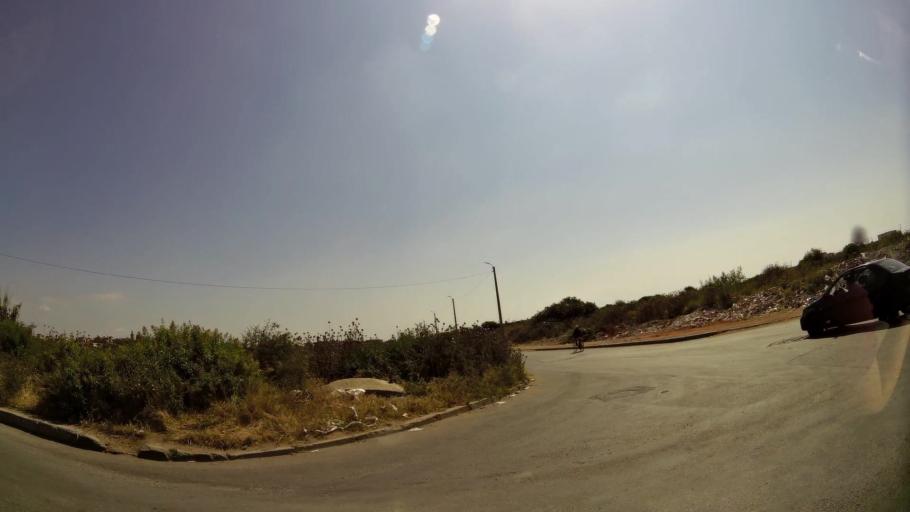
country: MA
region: Rabat-Sale-Zemmour-Zaer
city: Sale
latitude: 34.0810
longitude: -6.7564
